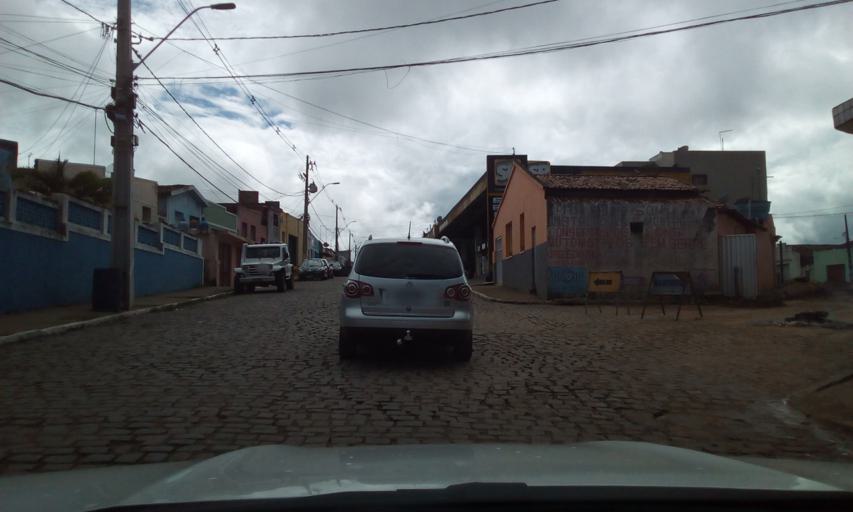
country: BR
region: Paraiba
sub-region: Areia
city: Areia
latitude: -6.9703
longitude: -35.6983
